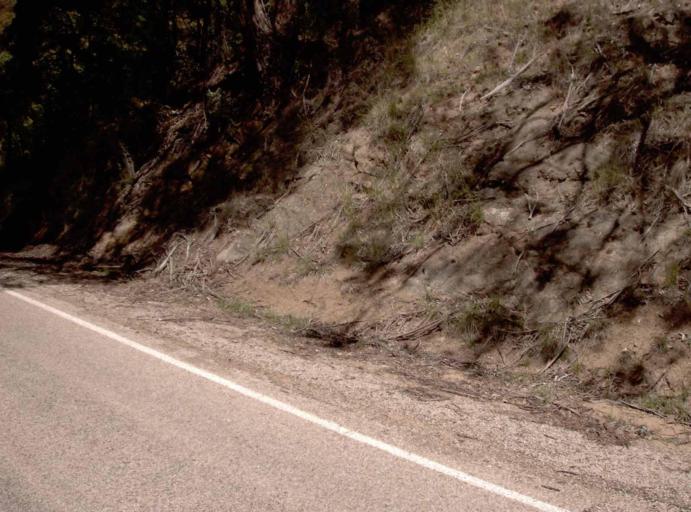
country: AU
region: Victoria
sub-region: Alpine
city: Mount Beauty
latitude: -37.1642
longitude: 147.6578
